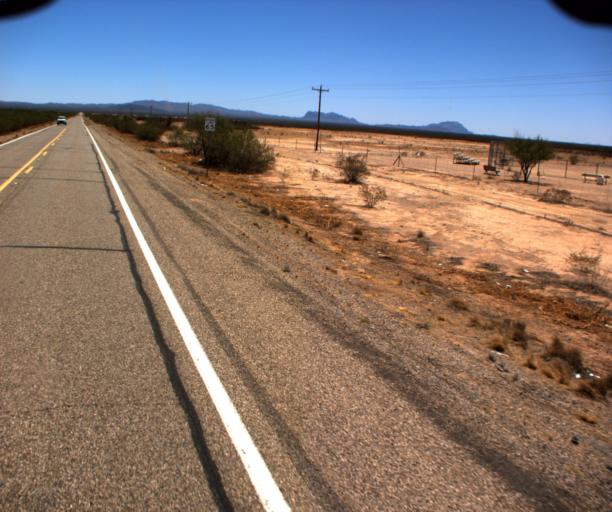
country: US
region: Arizona
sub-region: Pima County
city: Ajo
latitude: 32.1883
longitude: -112.3958
